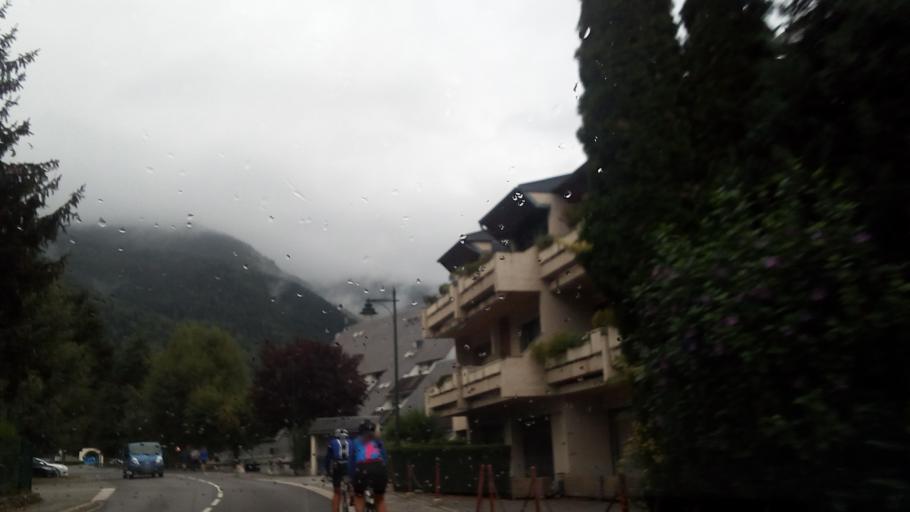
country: FR
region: Midi-Pyrenees
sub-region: Departement des Hautes-Pyrenees
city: Saint-Lary-Soulan
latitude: 42.8213
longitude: 0.3226
